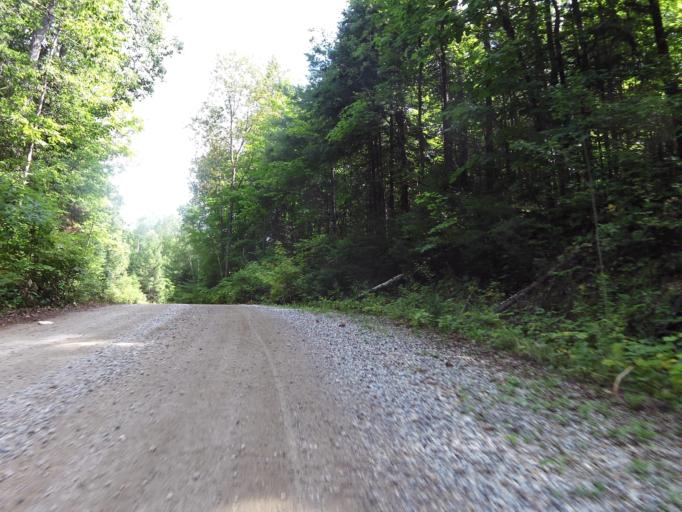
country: CA
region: Ontario
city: Renfrew
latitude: 45.1219
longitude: -76.7214
